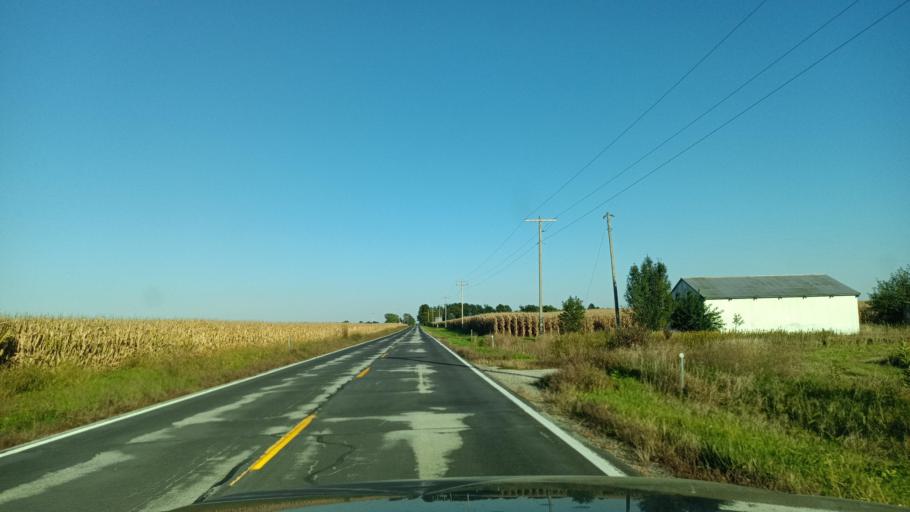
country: US
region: Illinois
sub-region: Mercer County
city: Aledo
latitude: 41.0678
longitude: -90.6925
